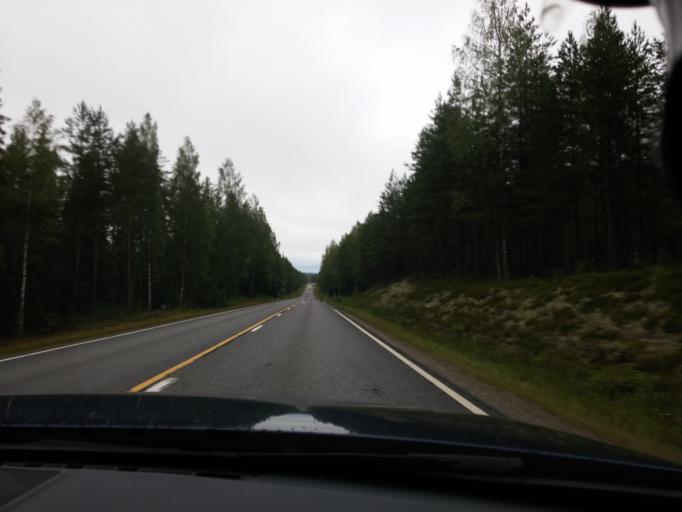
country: FI
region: Pirkanmaa
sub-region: Ylae-Pirkanmaa
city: Vilppula
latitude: 61.9360
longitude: 24.5406
